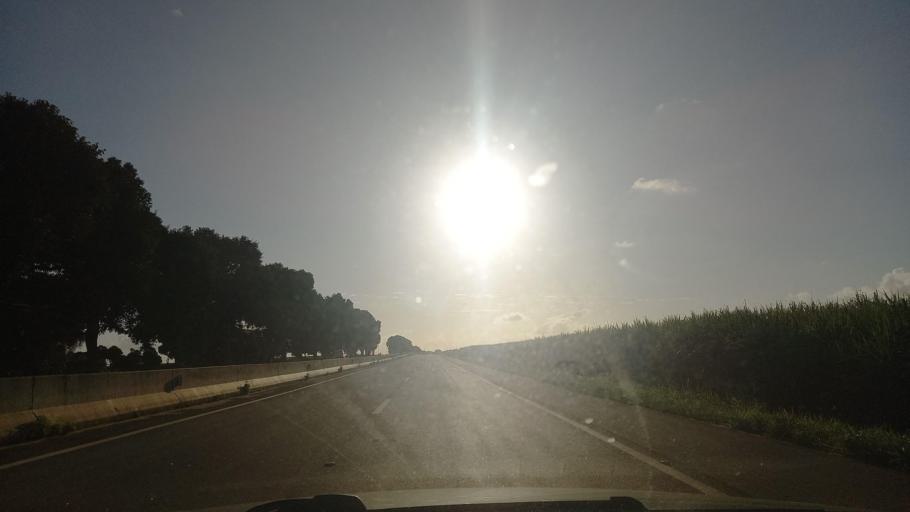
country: BR
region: Alagoas
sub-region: Campo Alegre
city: Campo Alegre
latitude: -9.7966
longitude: -36.3023
